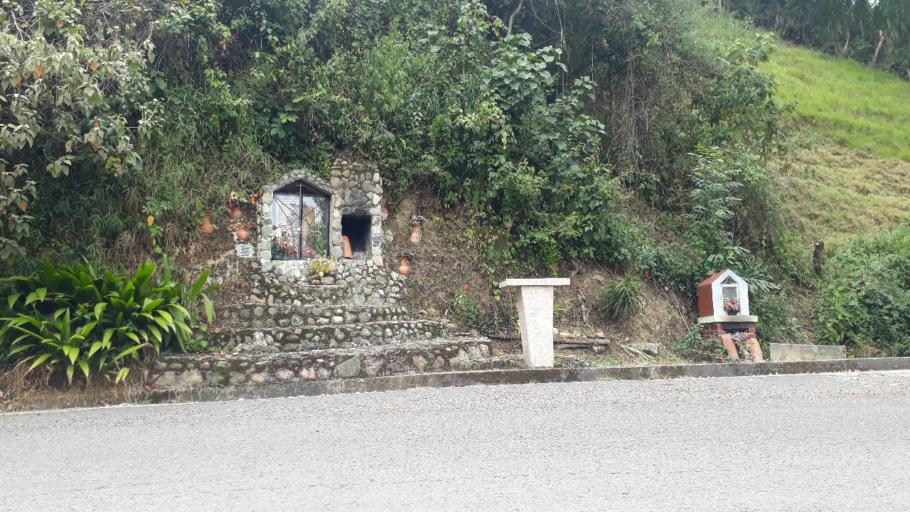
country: CO
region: Boyaca
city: San Mateo
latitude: 6.3929
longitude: -72.5600
